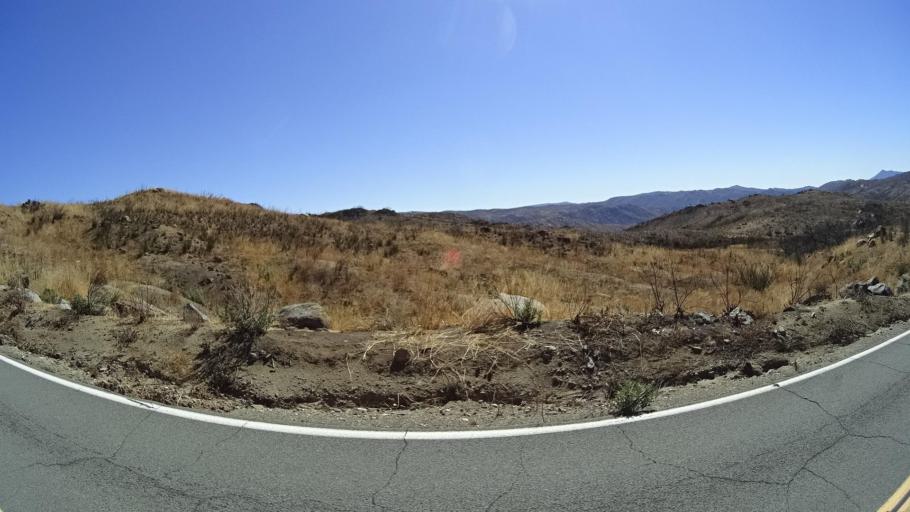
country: US
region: California
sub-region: San Diego County
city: Alpine
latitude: 32.7366
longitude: -116.6908
